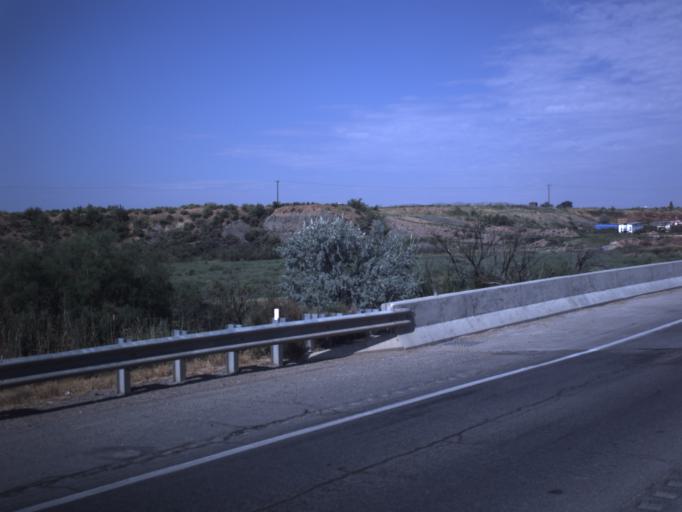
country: US
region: Utah
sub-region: Uintah County
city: Naples
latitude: 40.3748
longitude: -109.4075
